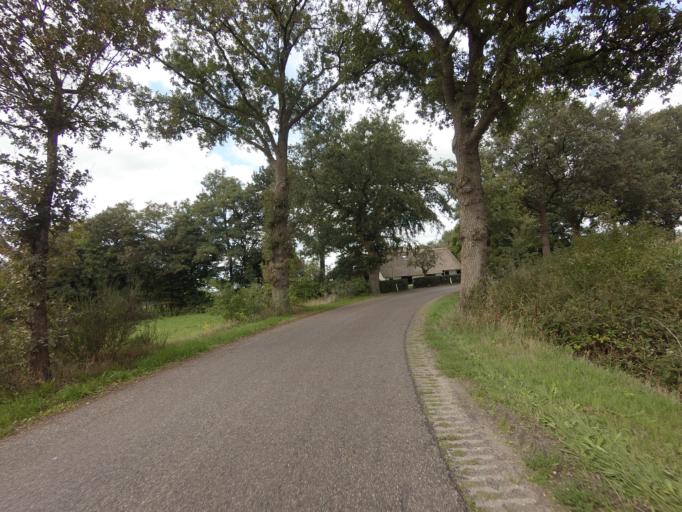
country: NL
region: Drenthe
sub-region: Gemeente De Wolden
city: Ruinen
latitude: 52.7380
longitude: 6.3410
